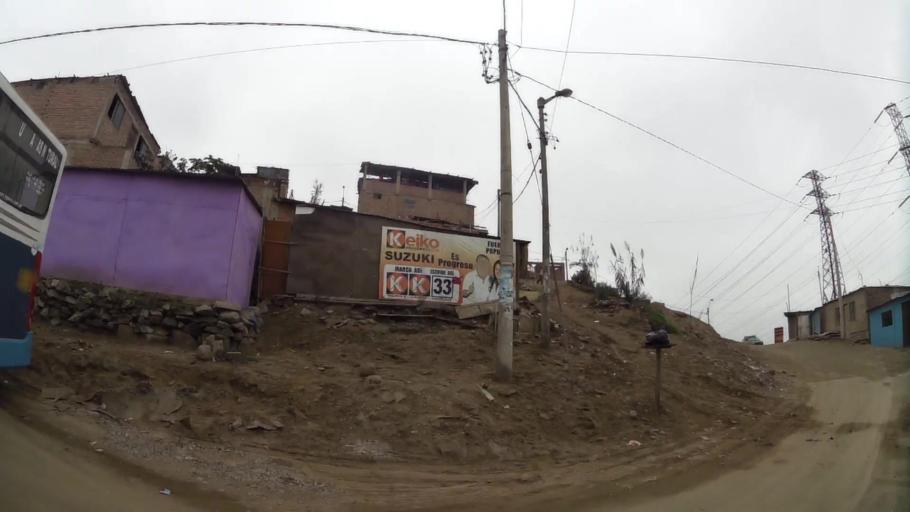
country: PE
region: Lima
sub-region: Lima
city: Surco
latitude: -12.1819
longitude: -76.9535
